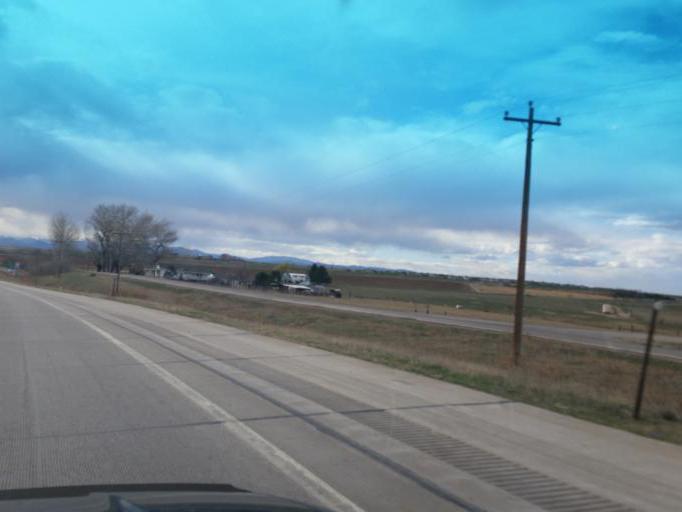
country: US
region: Colorado
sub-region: Weld County
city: Milliken
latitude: 40.4066
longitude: -104.8268
